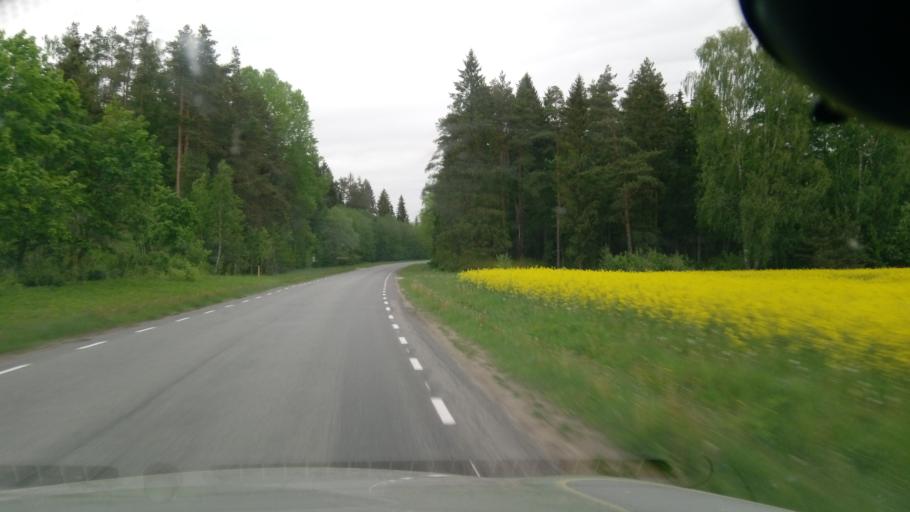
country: EE
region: Jaervamaa
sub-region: Koeru vald
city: Koeru
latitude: 58.9858
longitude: 26.0499
